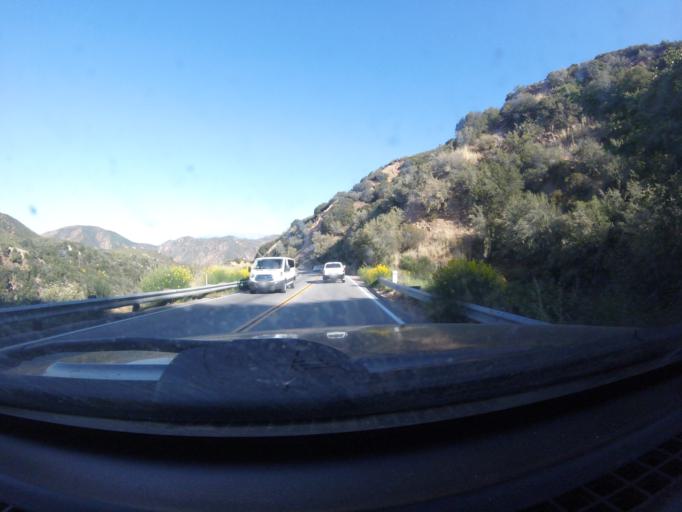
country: US
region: California
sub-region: San Bernardino County
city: Running Springs
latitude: 34.1788
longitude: -117.1578
